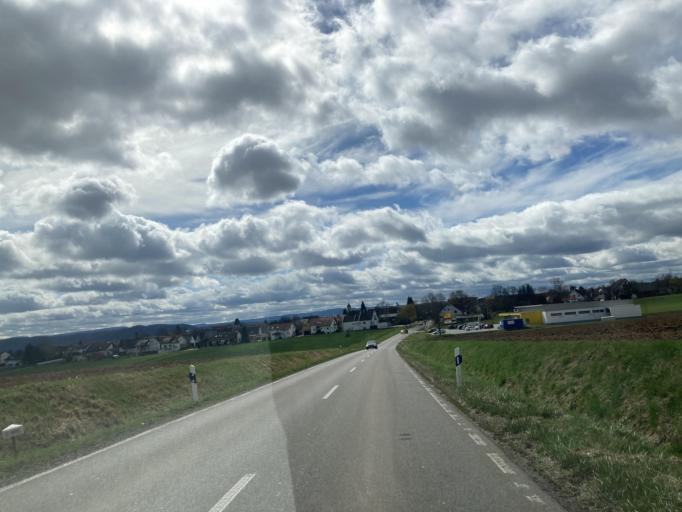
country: DE
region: Baden-Wuerttemberg
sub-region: Regierungsbezirk Stuttgart
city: Bondorf
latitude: 48.4882
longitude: 8.8811
